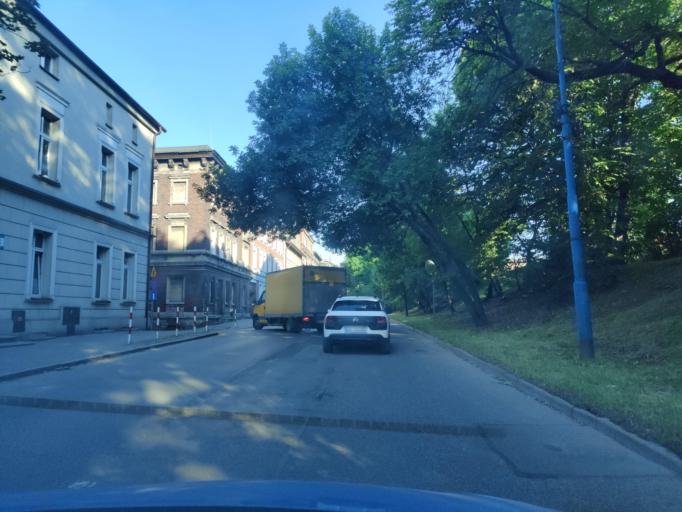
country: PL
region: Silesian Voivodeship
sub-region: Sosnowiec
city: Sosnowiec
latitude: 50.2462
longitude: 19.1333
